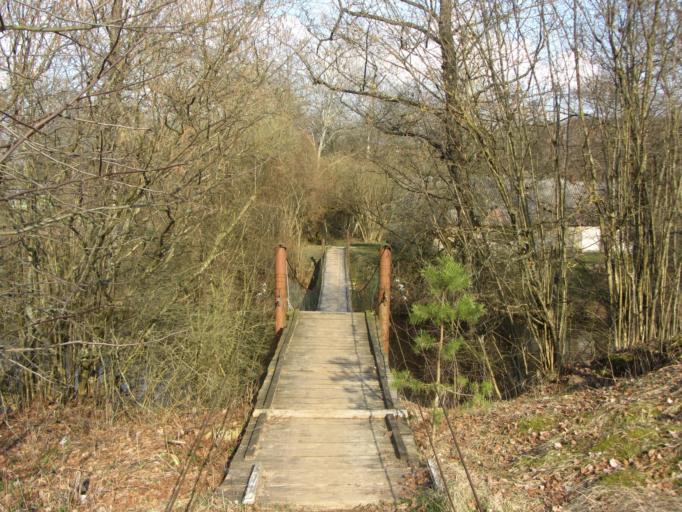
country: LT
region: Alytaus apskritis
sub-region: Alytaus rajonas
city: Daugai
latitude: 54.1887
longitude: 24.3744
